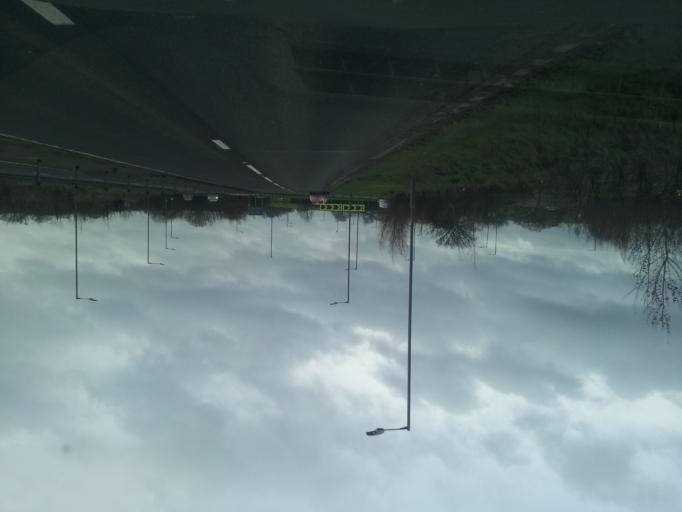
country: GB
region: England
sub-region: Central Bedfordshire
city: Leighton Buzzard
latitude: 51.9356
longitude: -0.6987
